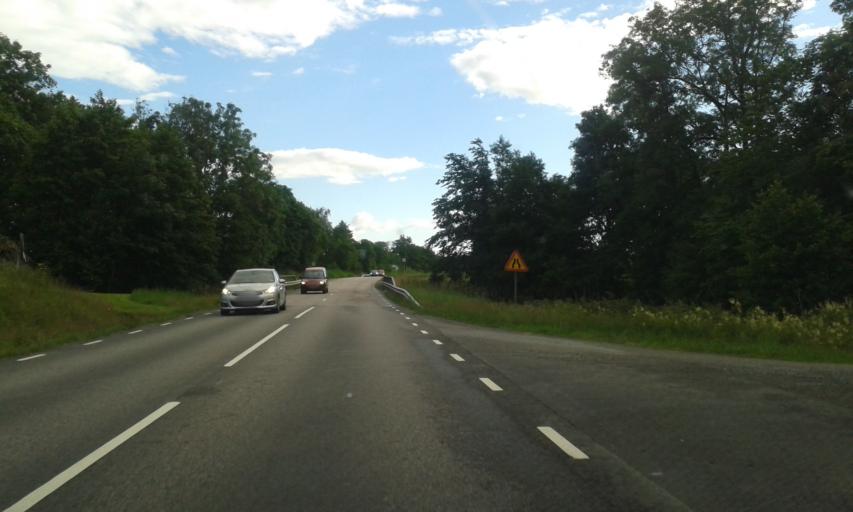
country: SE
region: Vaestra Goetaland
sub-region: Ale Kommun
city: Alafors
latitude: 57.9526
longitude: 12.0745
